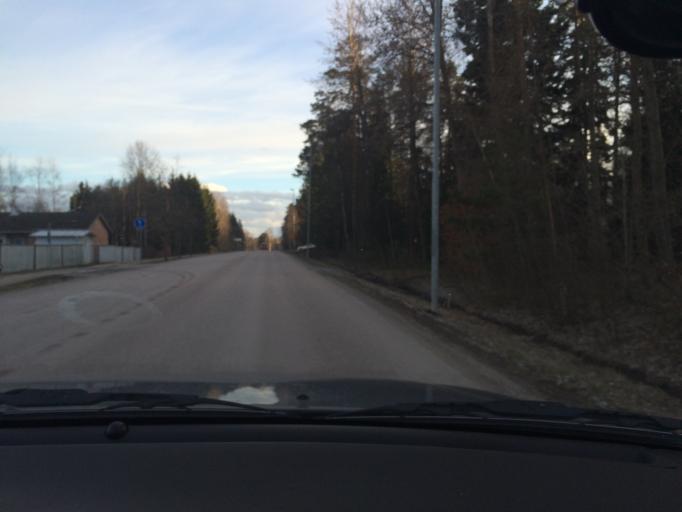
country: SE
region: Vaestmanland
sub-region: Vasteras
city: Vasteras
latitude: 59.6181
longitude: 16.5885
